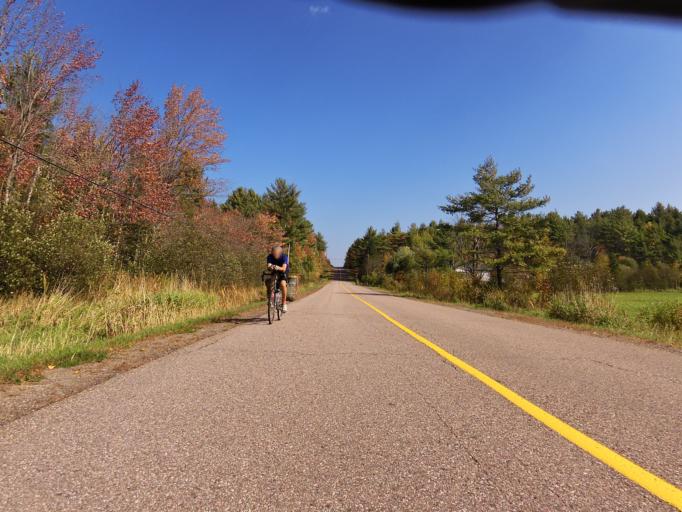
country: CA
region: Ontario
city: Petawawa
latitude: 45.8134
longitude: -77.2582
